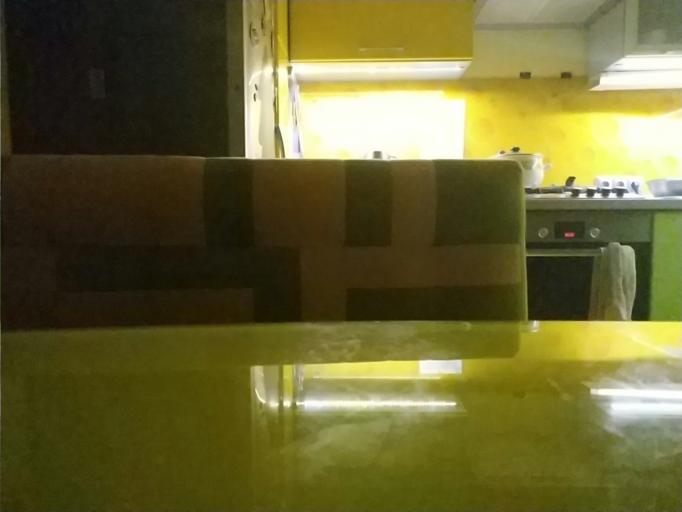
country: RU
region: Republic of Karelia
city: Kalevala
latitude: 65.3255
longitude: 30.6899
